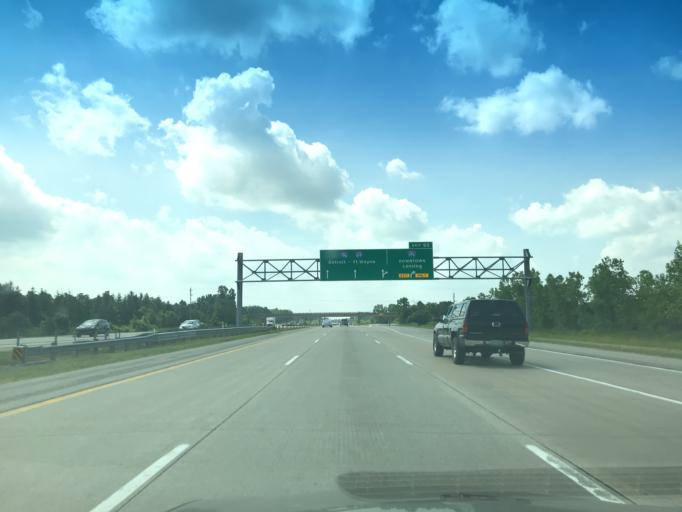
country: US
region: Michigan
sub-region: Eaton County
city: Waverly
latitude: 42.7302
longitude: -84.6688
